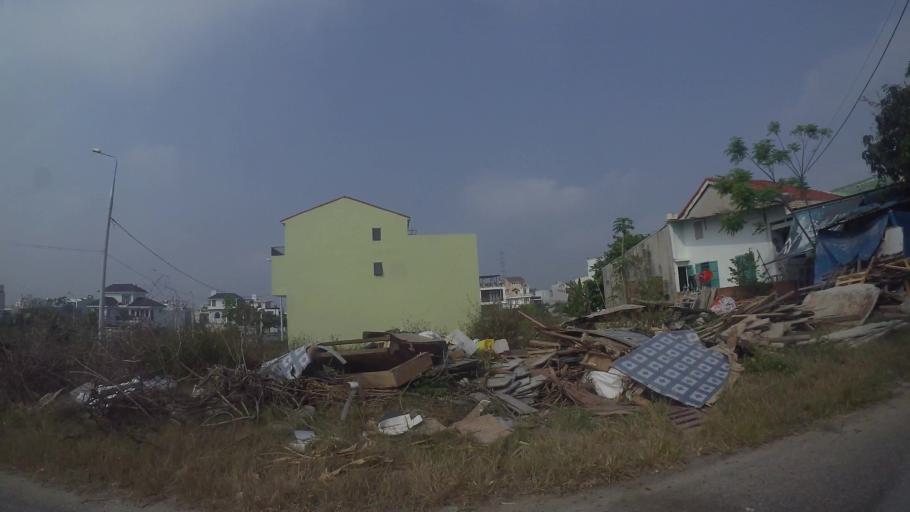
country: VN
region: Da Nang
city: Ngu Hanh Son
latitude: 16.0246
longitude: 108.2455
